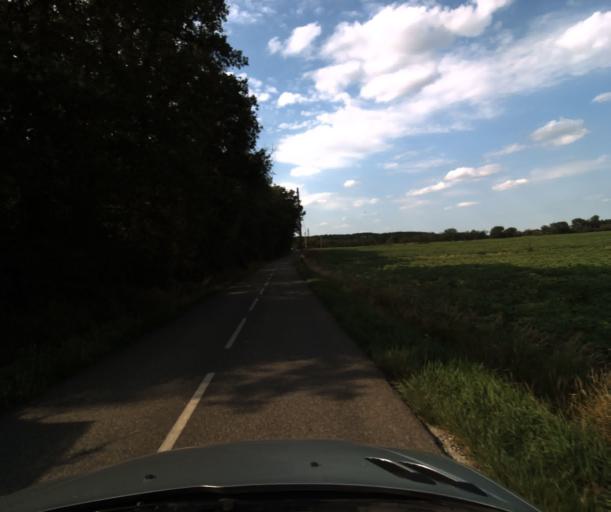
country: FR
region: Midi-Pyrenees
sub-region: Departement de la Haute-Garonne
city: Fonsorbes
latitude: 43.5130
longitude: 1.2212
